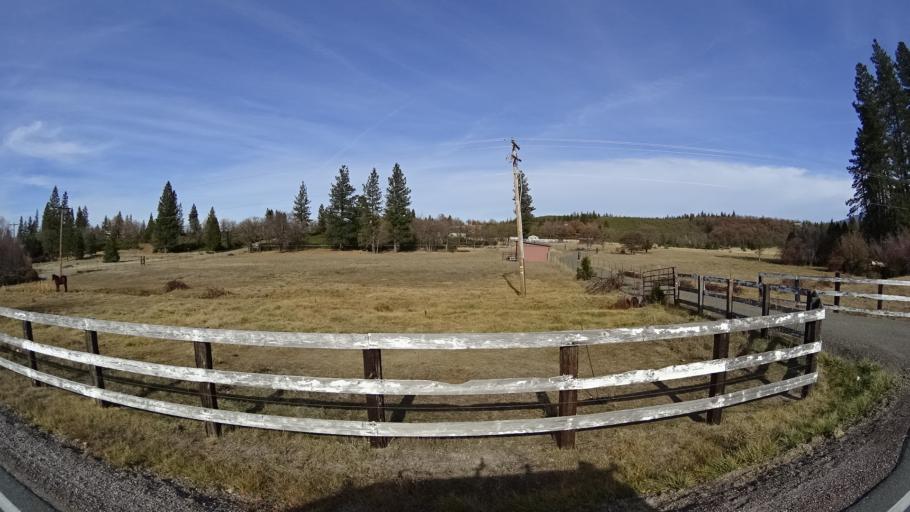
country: US
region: California
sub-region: Siskiyou County
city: Weed
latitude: 41.4018
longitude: -122.4233
